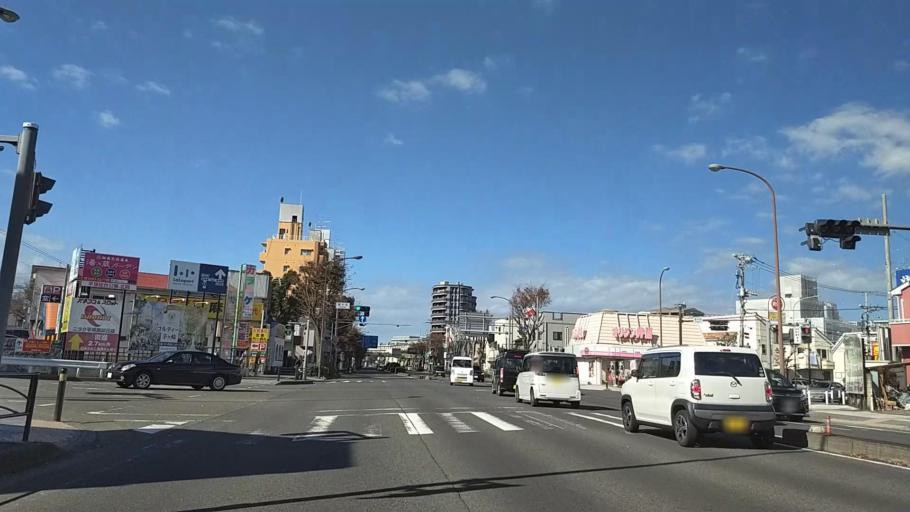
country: JP
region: Kanagawa
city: Hiratsuka
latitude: 35.3322
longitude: 139.3589
